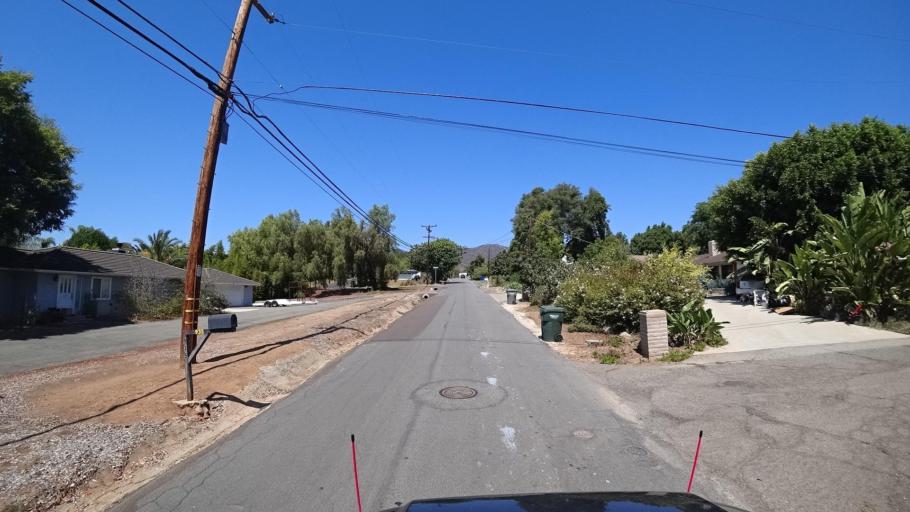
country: US
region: California
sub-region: San Diego County
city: San Marcos
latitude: 33.1923
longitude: -117.1857
